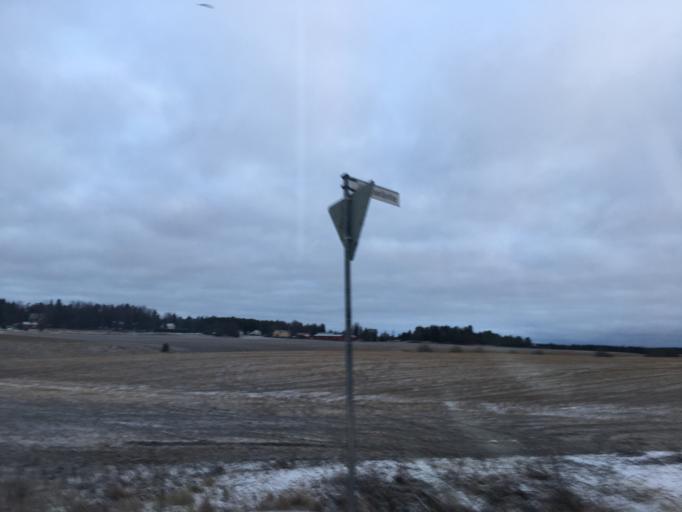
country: FI
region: Varsinais-Suomi
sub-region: Loimaa
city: Aura
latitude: 60.5869
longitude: 22.5347
